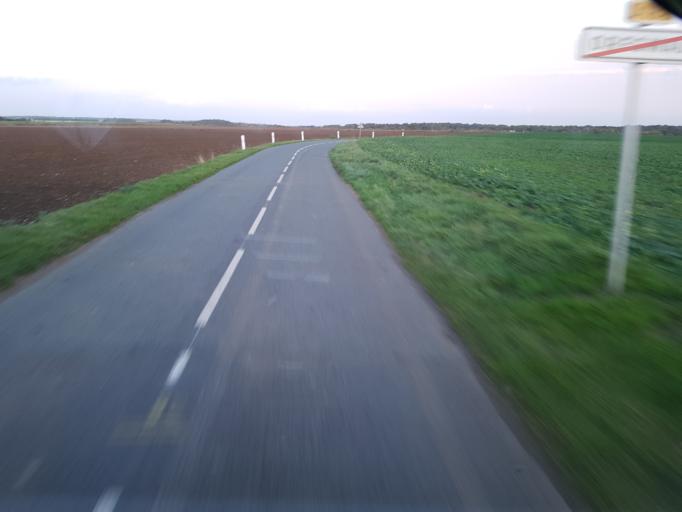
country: FR
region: Picardie
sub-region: Departement de la Somme
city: Sains-en-Amienois
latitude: 49.7679
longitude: 2.2762
